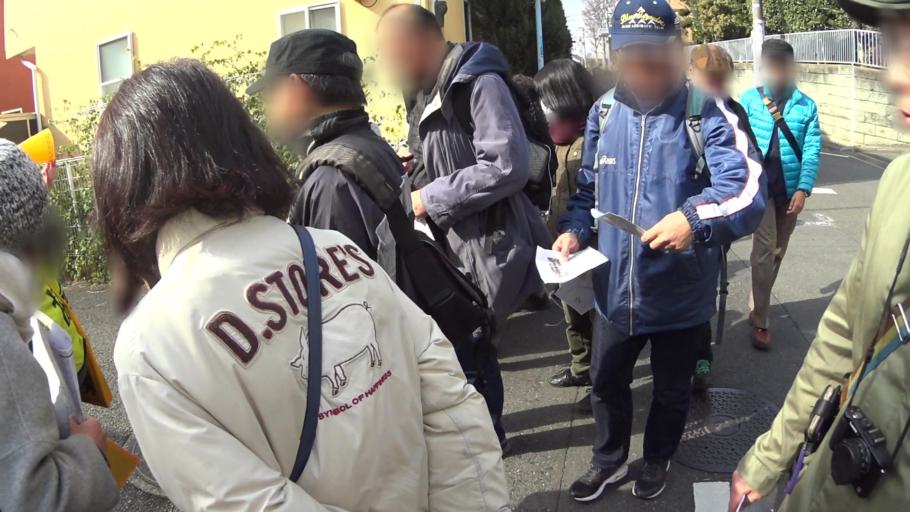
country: JP
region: Tokyo
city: Mitaka-shi
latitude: 35.6923
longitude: 139.5900
